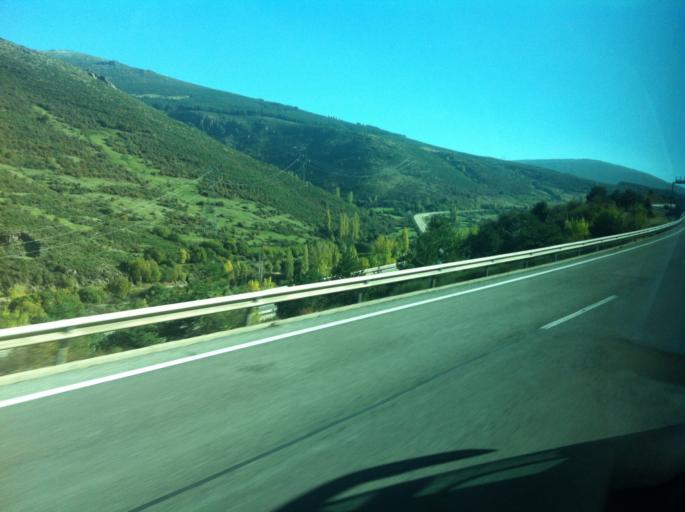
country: ES
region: Madrid
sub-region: Provincia de Madrid
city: Somosierra
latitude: 41.1534
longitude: -3.5852
